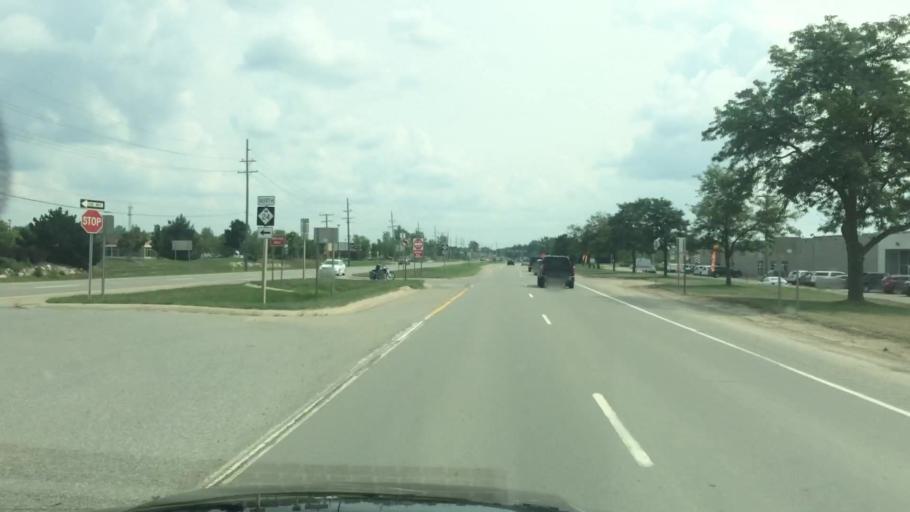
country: US
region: Michigan
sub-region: Oakland County
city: Oxford
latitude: 42.8400
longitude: -83.2739
